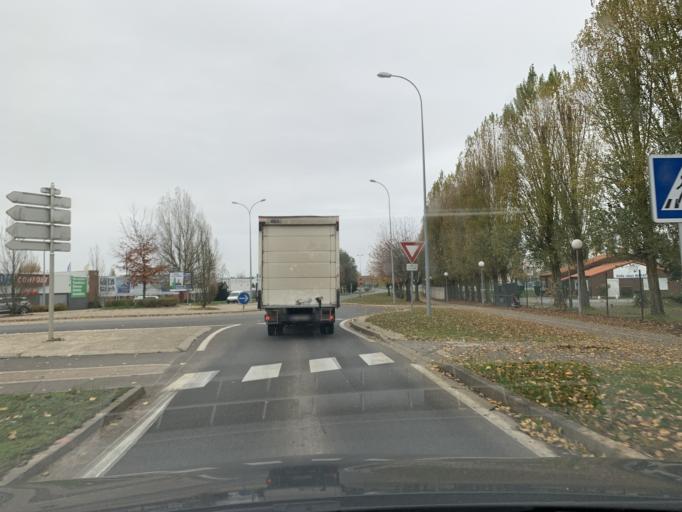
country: FR
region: Nord-Pas-de-Calais
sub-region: Departement du Nord
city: Neuville-Saint-Remy
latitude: 50.1923
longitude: 3.2131
